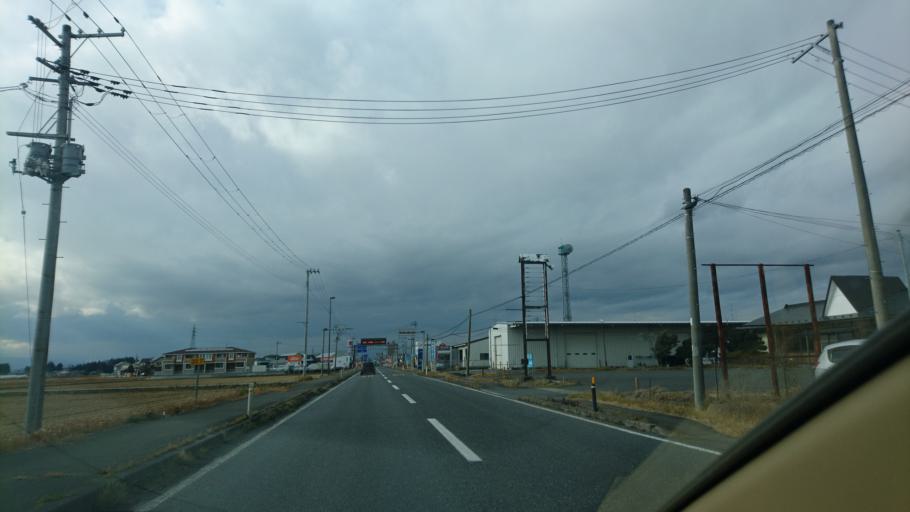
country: JP
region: Miyagi
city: Furukawa
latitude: 38.5677
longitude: 140.9962
